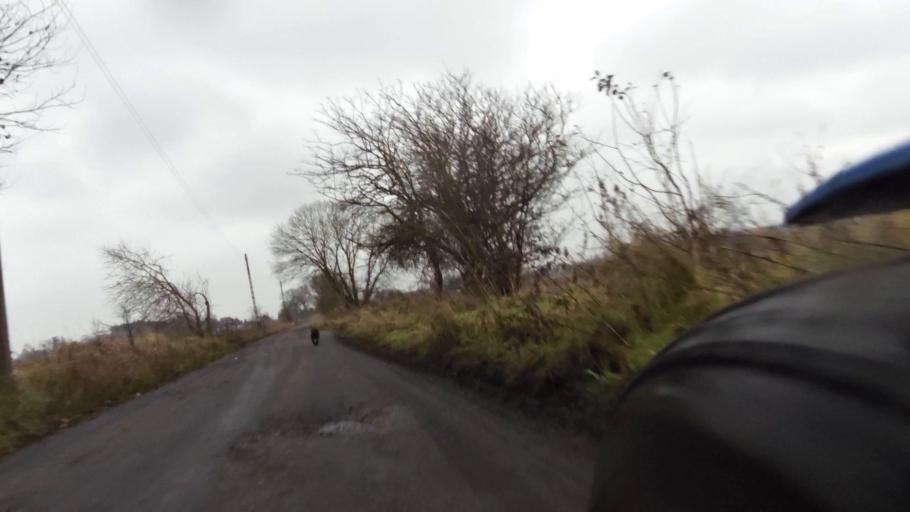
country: PL
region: West Pomeranian Voivodeship
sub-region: Powiat szczecinecki
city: Szczecinek
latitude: 53.6647
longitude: 16.6649
